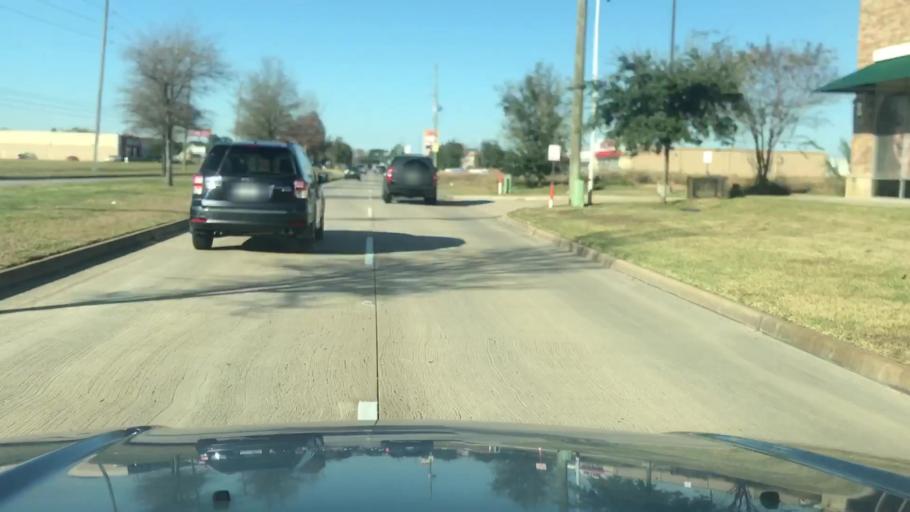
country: US
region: Texas
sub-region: Fort Bend County
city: Cinco Ranch
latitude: 29.8141
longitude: -95.7521
